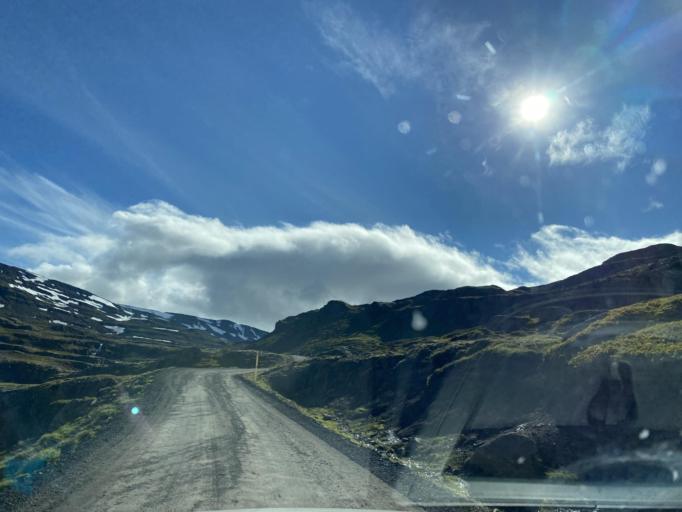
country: IS
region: East
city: Eskifjoerdur
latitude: 65.1781
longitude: -14.1066
